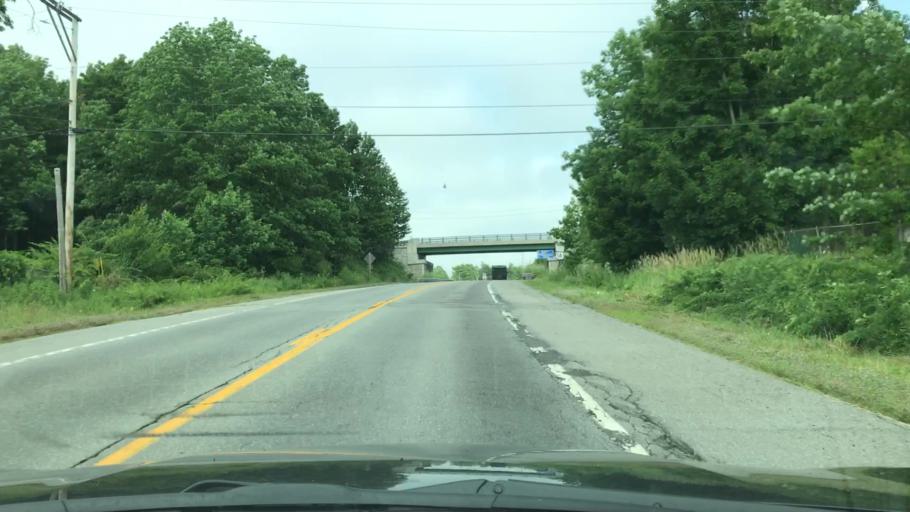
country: US
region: Maine
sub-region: Waldo County
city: Stockton Springs
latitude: 44.4908
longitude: -68.8590
